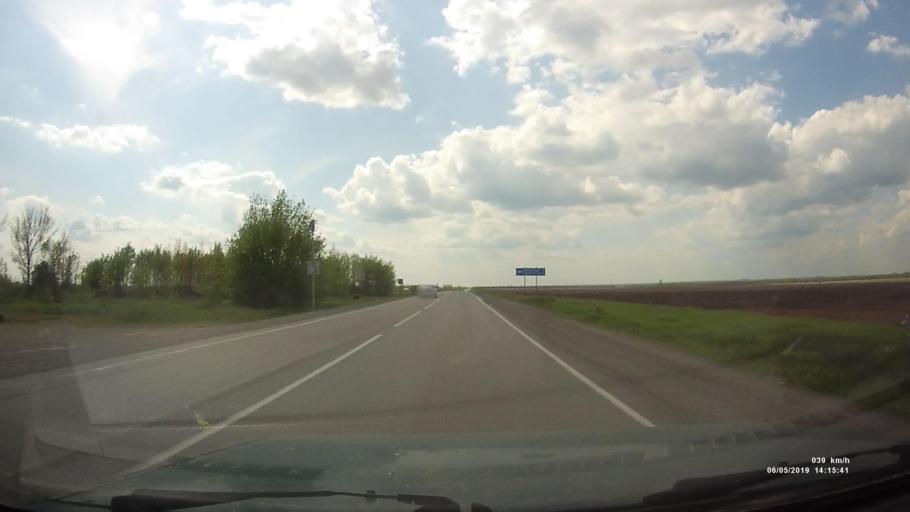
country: RU
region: Rostov
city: Kamenolomni
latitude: 47.6352
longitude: 40.3013
